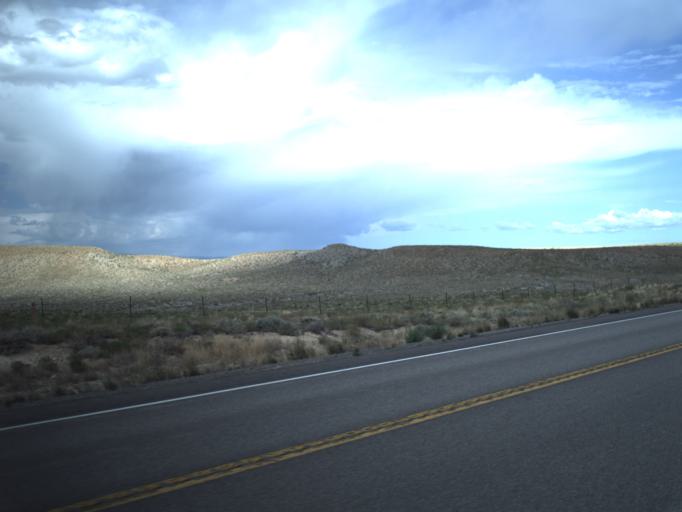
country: US
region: Utah
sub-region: Carbon County
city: East Carbon City
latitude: 39.4974
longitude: -110.5245
